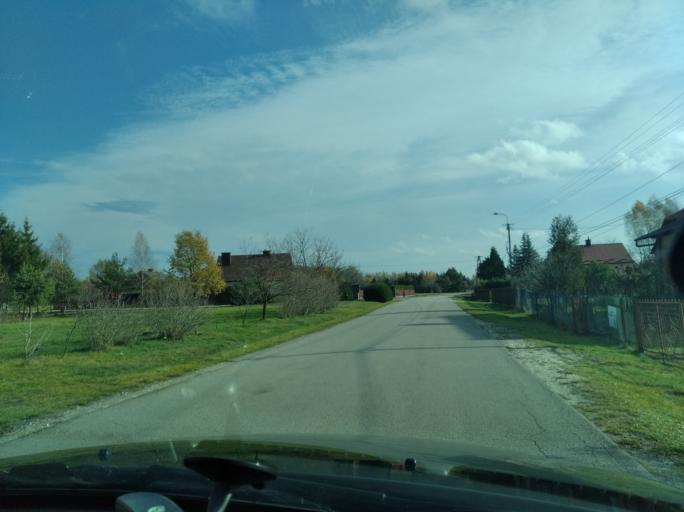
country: PL
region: Subcarpathian Voivodeship
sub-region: Powiat ropczycko-sedziszowski
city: Sedziszow Malopolski
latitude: 50.1196
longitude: 21.7253
